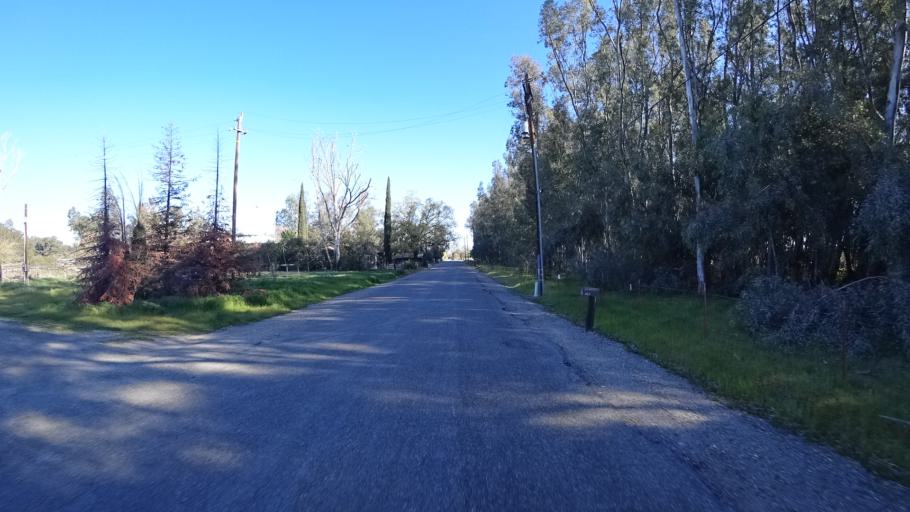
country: US
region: California
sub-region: Glenn County
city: Orland
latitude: 39.7665
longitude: -122.2155
